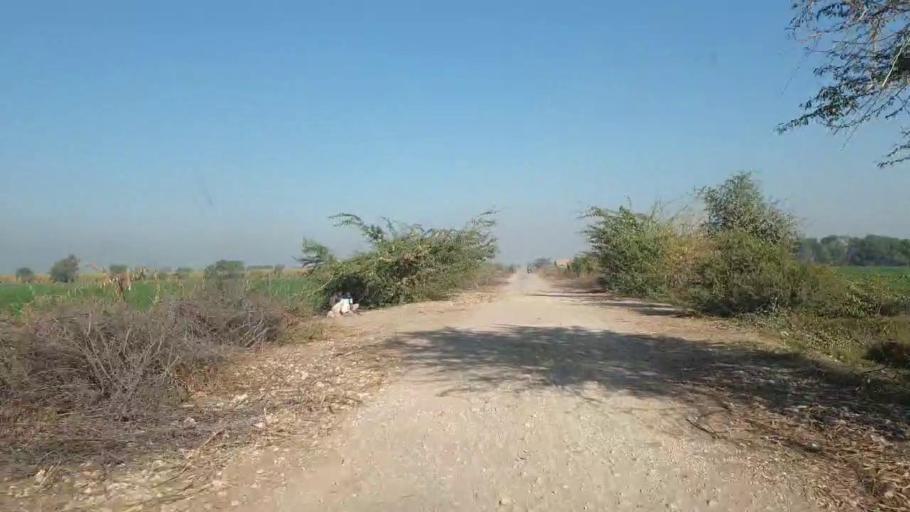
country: PK
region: Sindh
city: Shahdadpur
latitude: 25.9625
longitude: 68.4997
